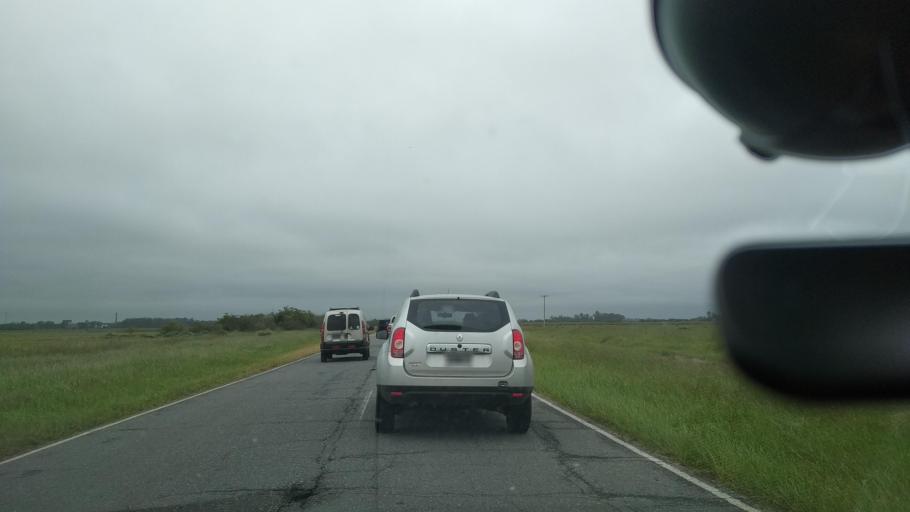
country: AR
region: Buenos Aires
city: Veronica
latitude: -35.5514
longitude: -57.3089
